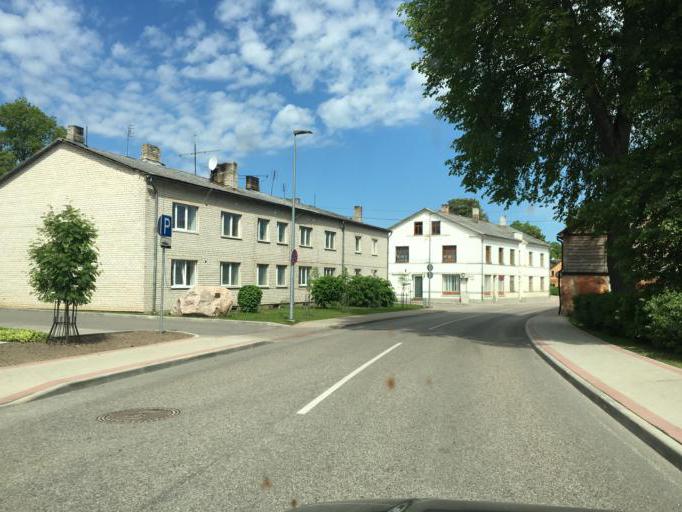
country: LV
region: Talsu Rajons
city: Valdemarpils
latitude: 57.3727
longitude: 22.5908
